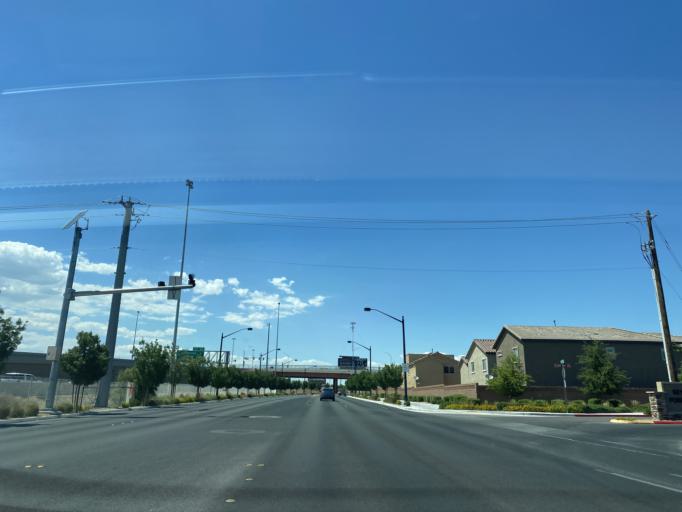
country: US
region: Nevada
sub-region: Clark County
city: Summerlin South
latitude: 36.2898
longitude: -115.2773
